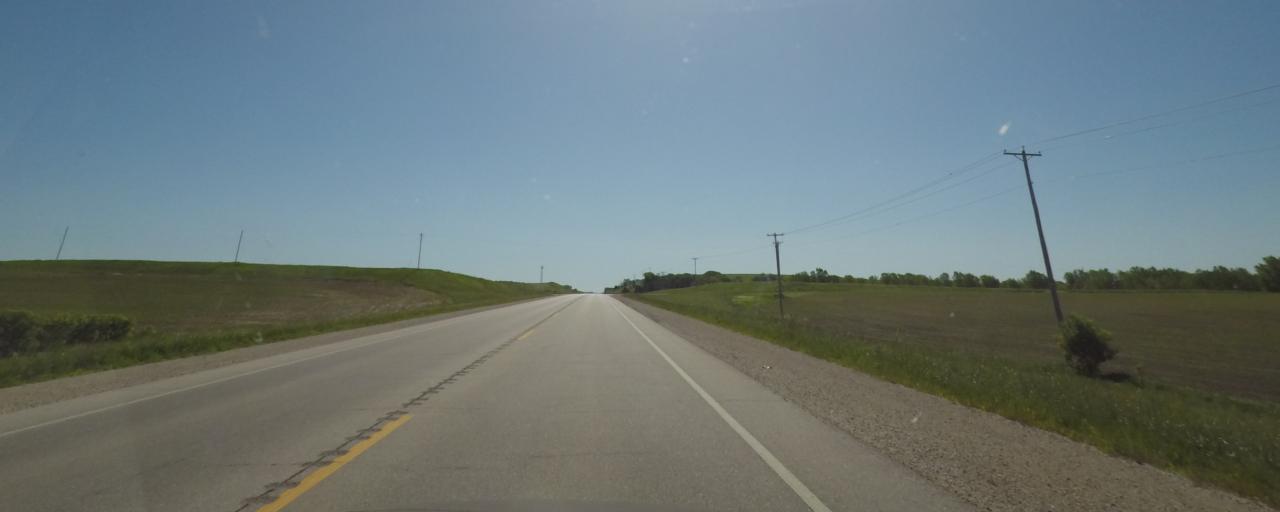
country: US
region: Wisconsin
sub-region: Fond du Lac County
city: Saint Peter
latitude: 43.7833
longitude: -88.3241
